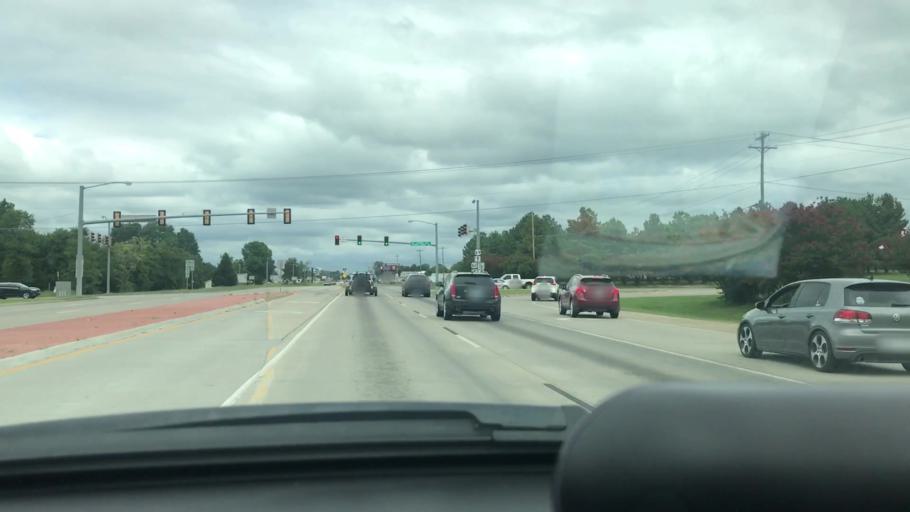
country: US
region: Oklahoma
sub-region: Muskogee County
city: Muskogee
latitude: 35.7687
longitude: -95.4024
